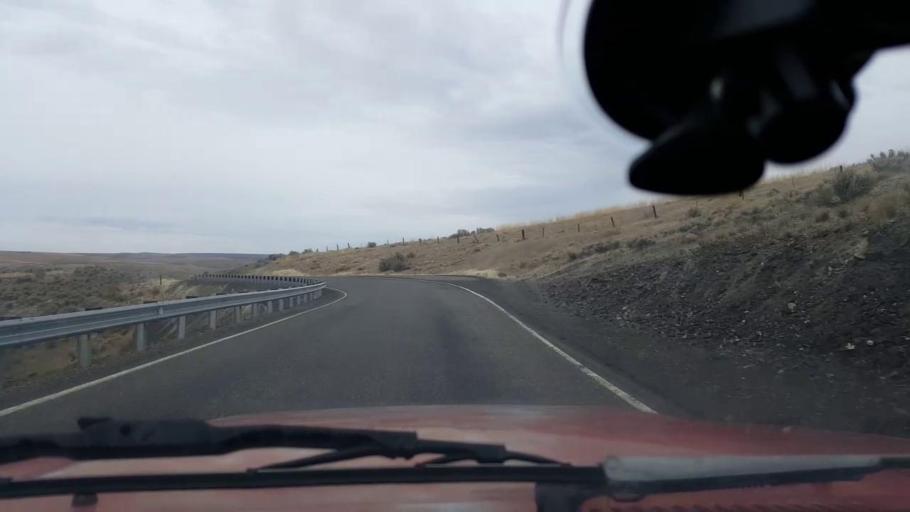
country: US
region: Washington
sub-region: Asotin County
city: Clarkston Heights-Vineland
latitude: 46.3343
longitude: -117.2825
